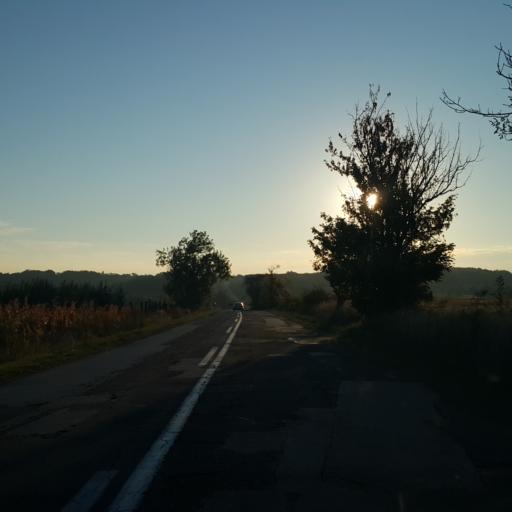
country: RS
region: Central Serbia
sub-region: Borski Okrug
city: Negotin
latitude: 44.2089
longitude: 22.4361
